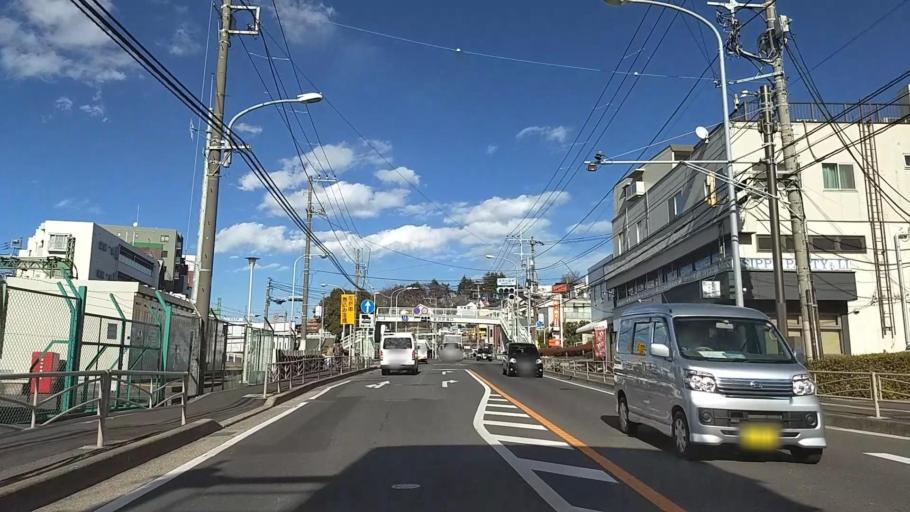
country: JP
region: Kanagawa
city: Zushi
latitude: 35.3591
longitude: 139.6289
